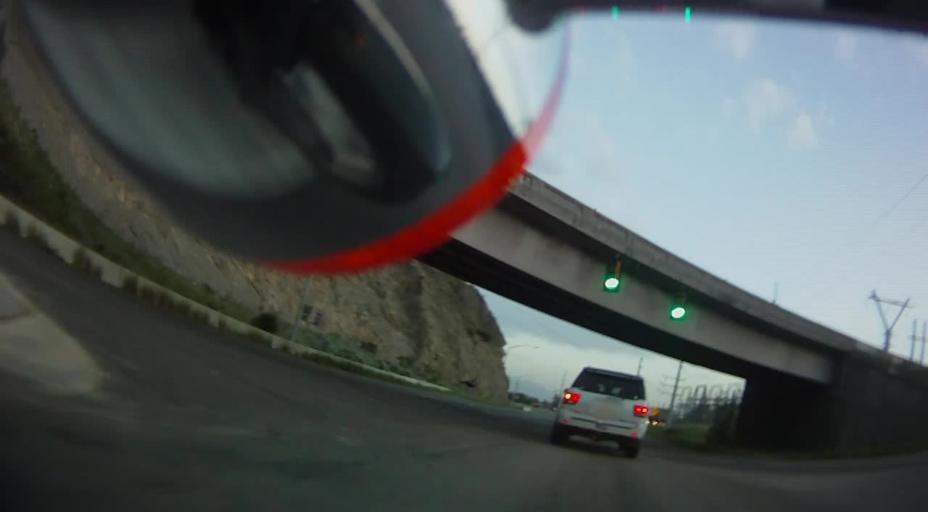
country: US
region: Utah
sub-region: Utah County
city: Orem
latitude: 40.3133
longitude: -111.6553
